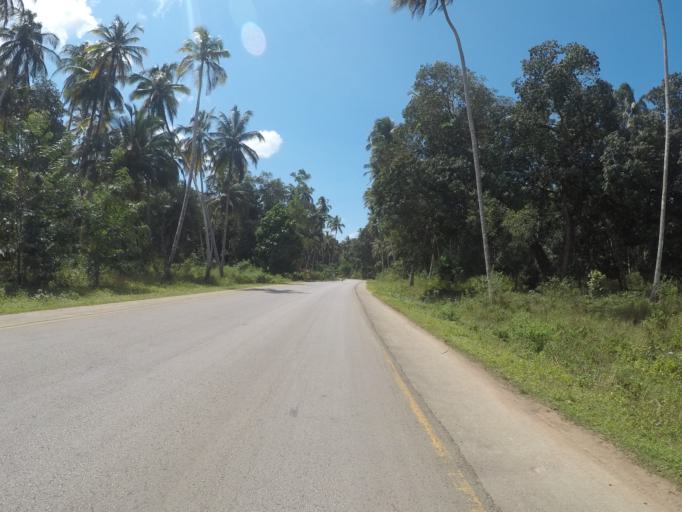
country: TZ
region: Zanzibar Central/South
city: Koani
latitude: -6.1495
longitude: 39.3293
